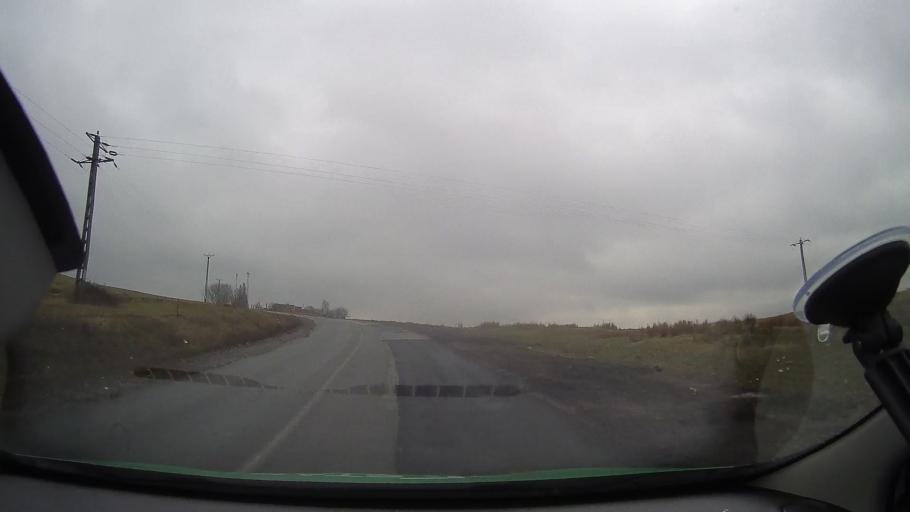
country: RO
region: Arad
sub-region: Comuna Halmagiu
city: Halmagiu
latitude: 46.2834
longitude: 22.5717
